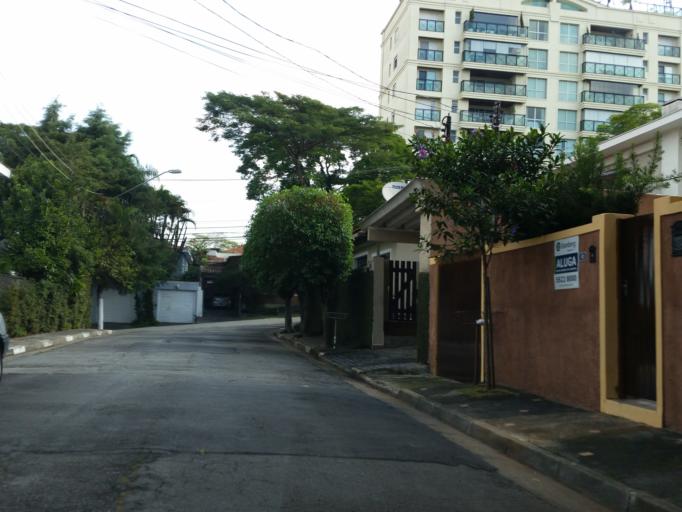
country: BR
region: Sao Paulo
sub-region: Diadema
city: Diadema
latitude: -23.6506
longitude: -46.6969
